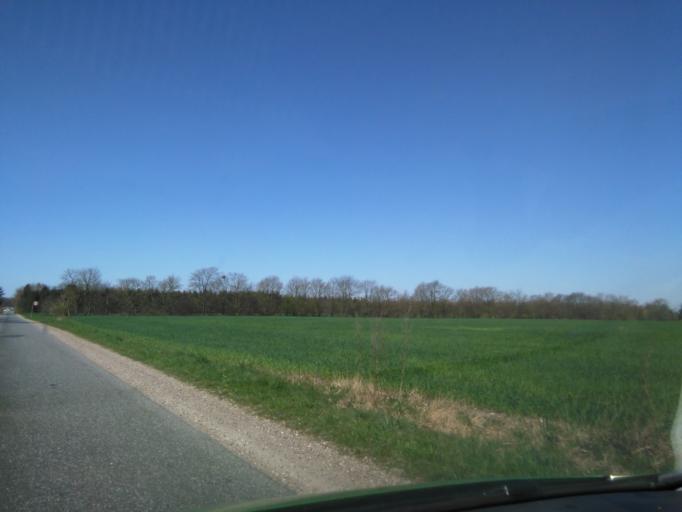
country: DK
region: South Denmark
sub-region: Billund Kommune
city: Billund
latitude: 55.7106
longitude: 9.1066
